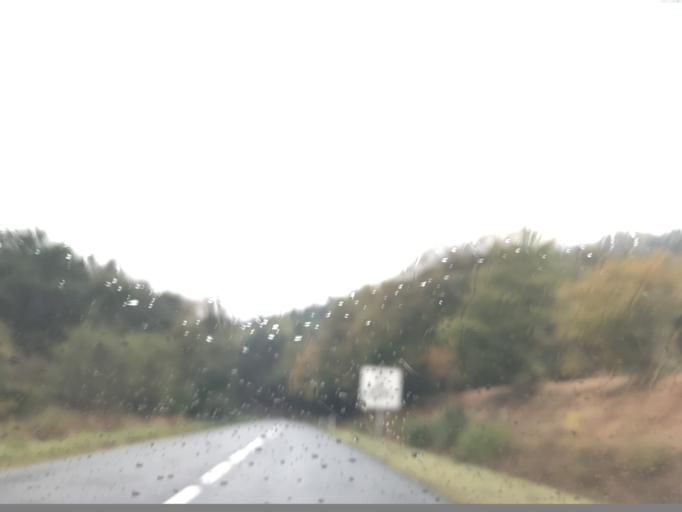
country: FR
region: Auvergne
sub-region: Departement du Puy-de-Dome
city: Lezoux
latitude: 45.7732
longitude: 3.4154
